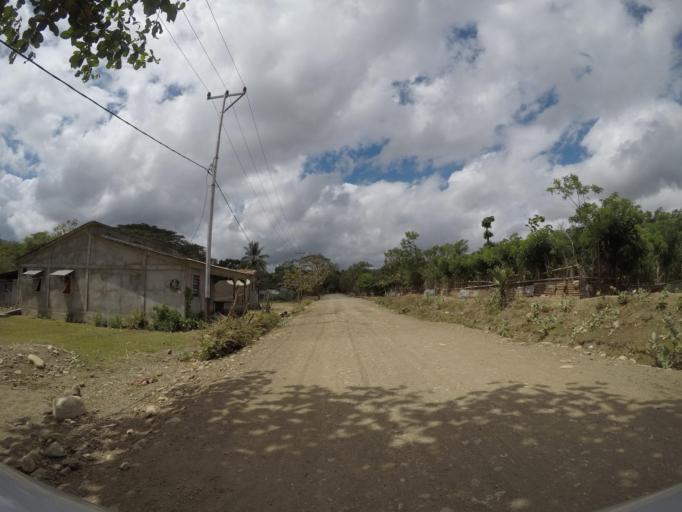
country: TL
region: Lautem
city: Lospalos
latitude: -8.5130
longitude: 126.8341
